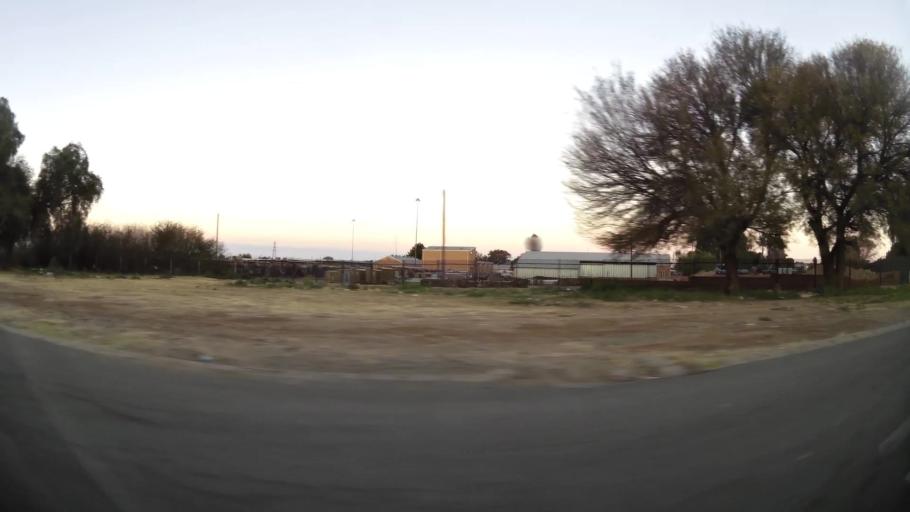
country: ZA
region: Northern Cape
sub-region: Frances Baard District Municipality
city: Kimberley
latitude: -28.7150
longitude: 24.7719
